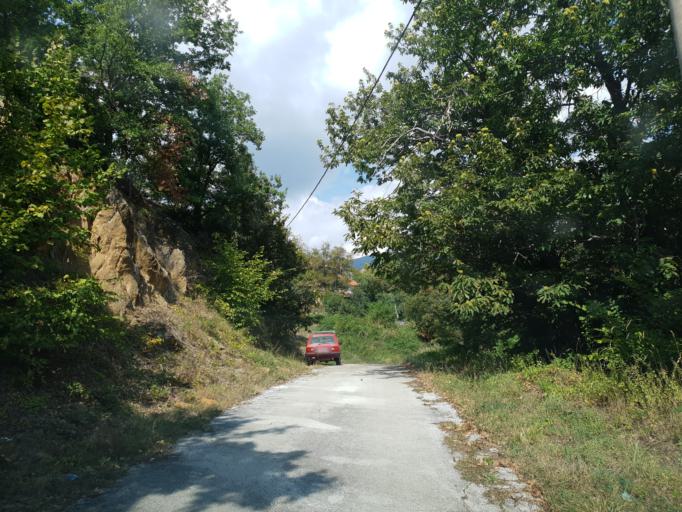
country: MK
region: Makedonski Brod
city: Samokov
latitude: 41.7455
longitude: 21.1046
